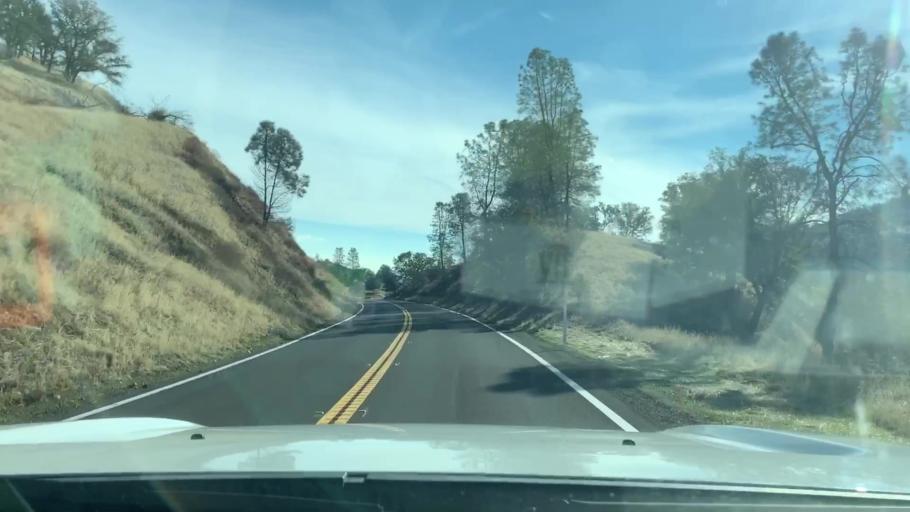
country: US
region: California
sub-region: Fresno County
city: Coalinga
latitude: 36.1116
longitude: -120.5668
